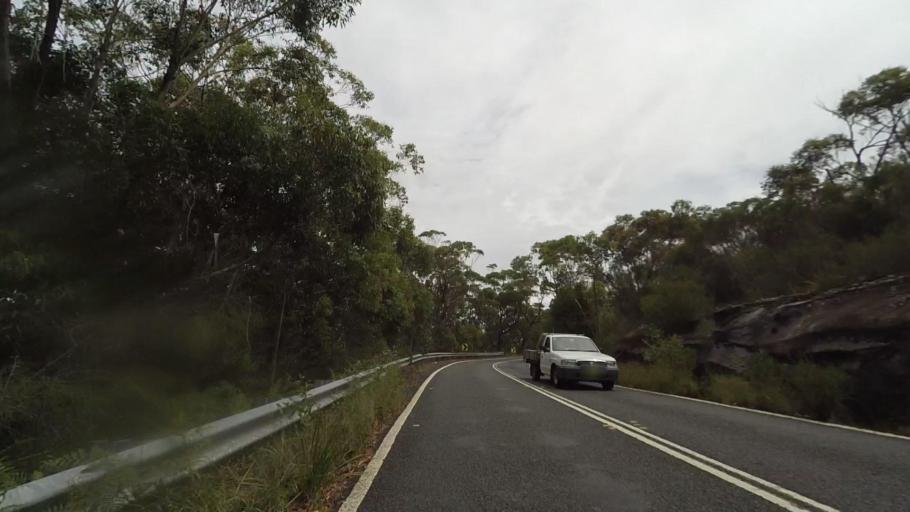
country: AU
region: New South Wales
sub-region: Sutherland Shire
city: Heathcote
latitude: -34.1156
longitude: 151.0634
